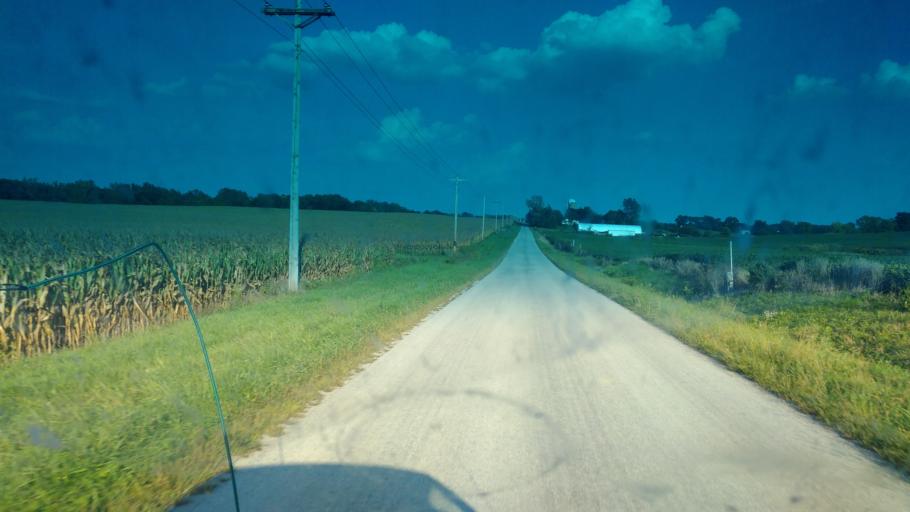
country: US
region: Ohio
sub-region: Wyandot County
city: Upper Sandusky
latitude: 40.9283
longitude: -83.1243
